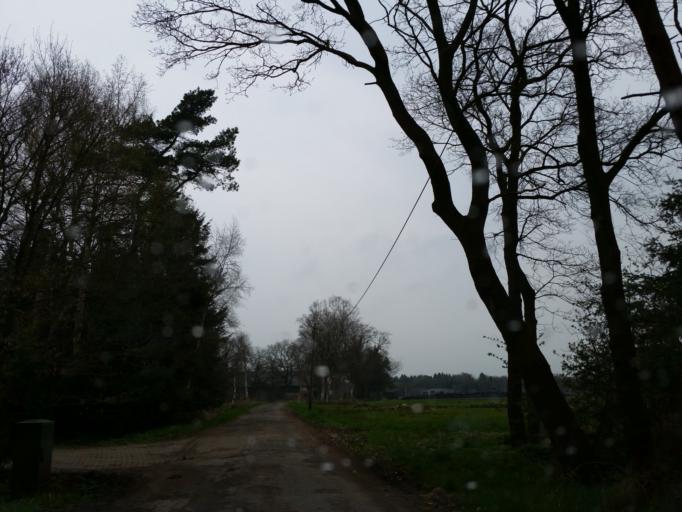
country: DE
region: Lower Saxony
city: Armstorf
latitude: 53.5860
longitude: 9.0081
